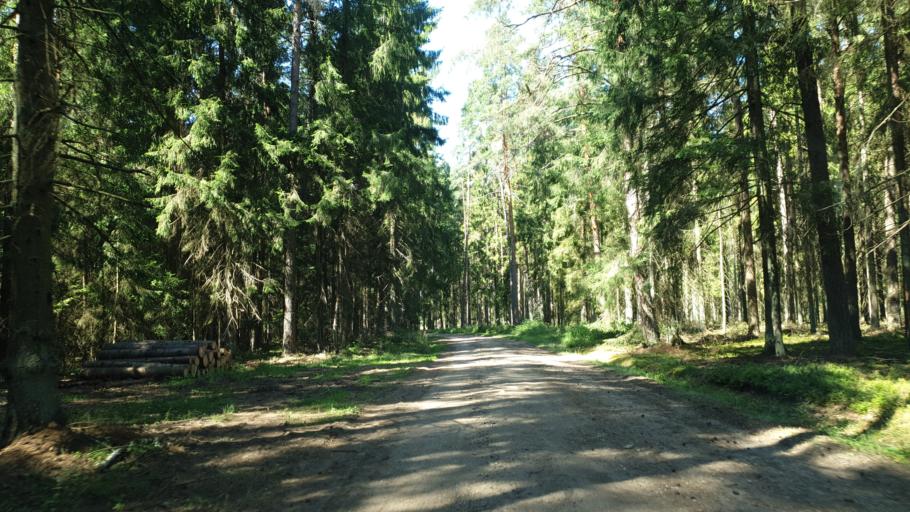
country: LT
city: Sirvintos
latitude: 54.9089
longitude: 24.9389
